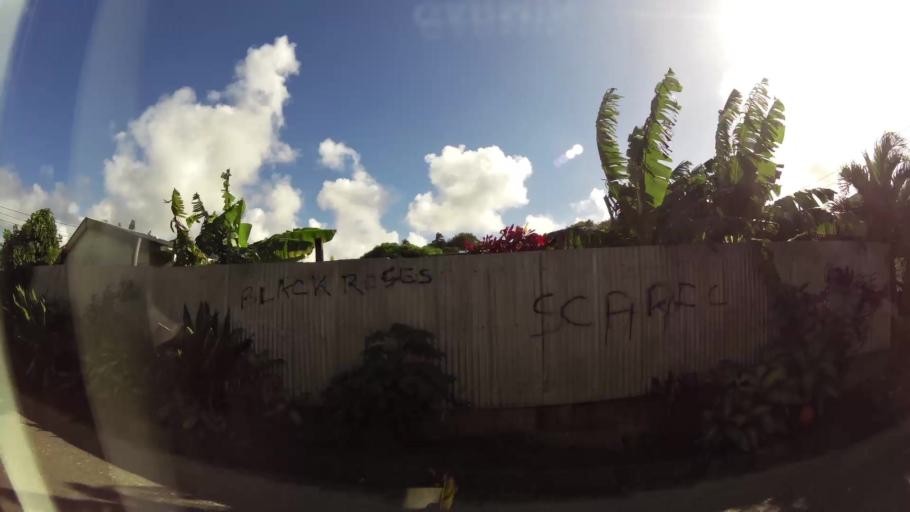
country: LC
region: Castries Quarter
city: Bisee
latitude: 14.0456
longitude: -60.9654
